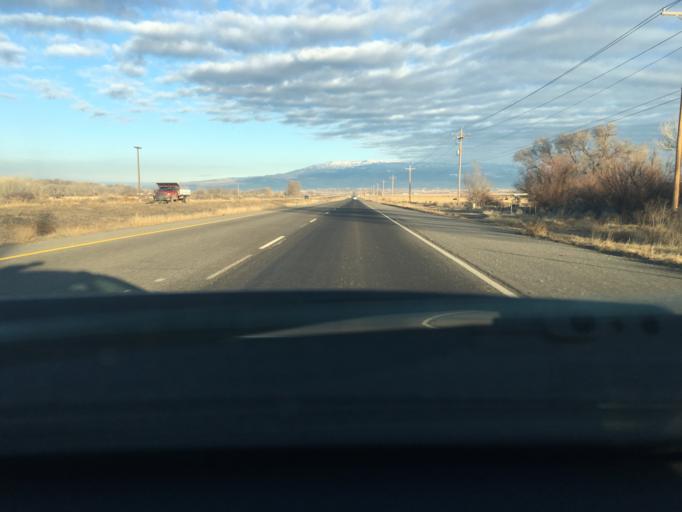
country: US
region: Colorado
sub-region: Montrose County
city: Olathe
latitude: 38.6737
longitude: -108.0026
